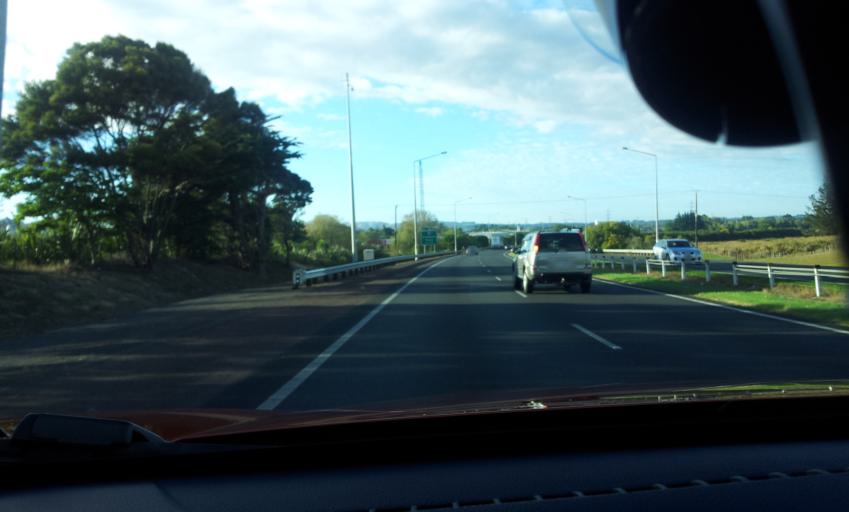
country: NZ
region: Auckland
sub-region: Auckland
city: Papakura
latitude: -37.0931
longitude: 174.9429
